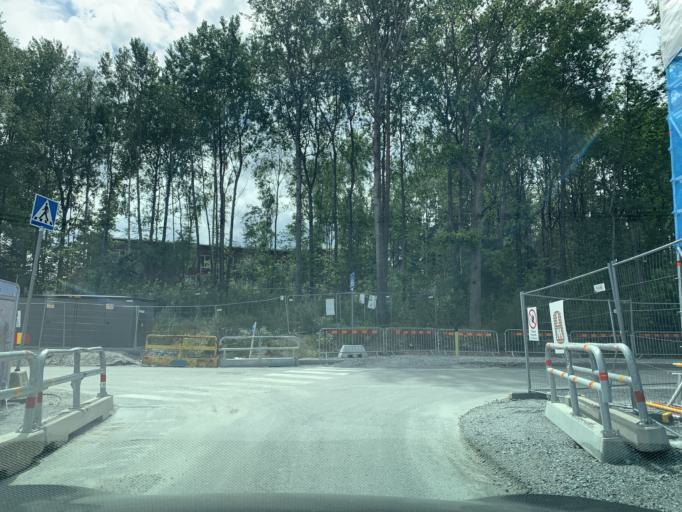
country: SE
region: Stockholm
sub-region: Solna Kommun
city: Rasunda
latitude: 59.3857
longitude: 17.9871
